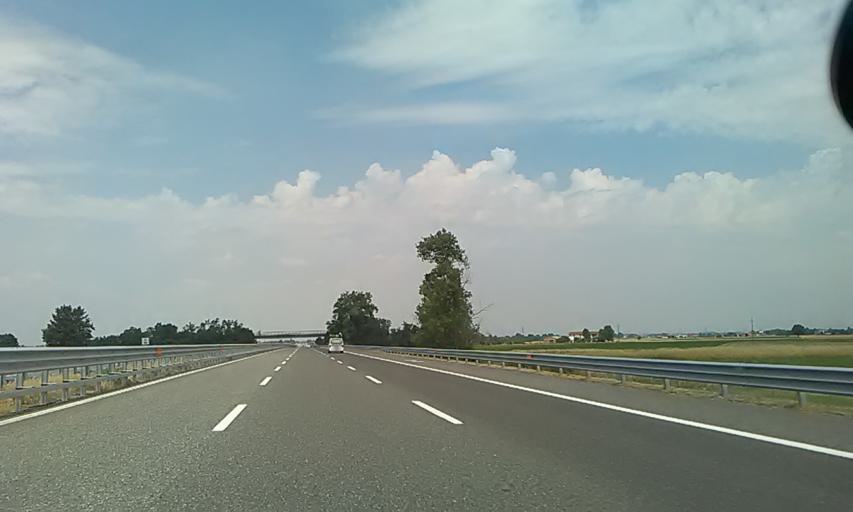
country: IT
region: Piedmont
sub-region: Provincia di Alessandria
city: Castelspina
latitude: 44.7844
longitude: 8.6193
